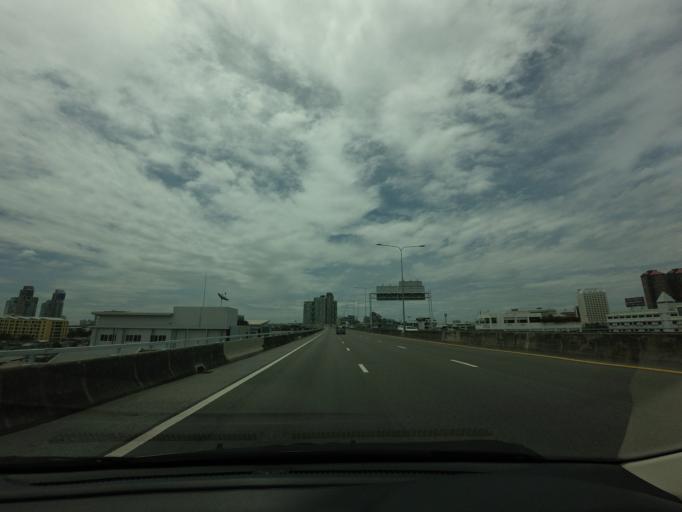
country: TH
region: Bangkok
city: Phra Khanong
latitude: 13.6800
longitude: 100.6036
